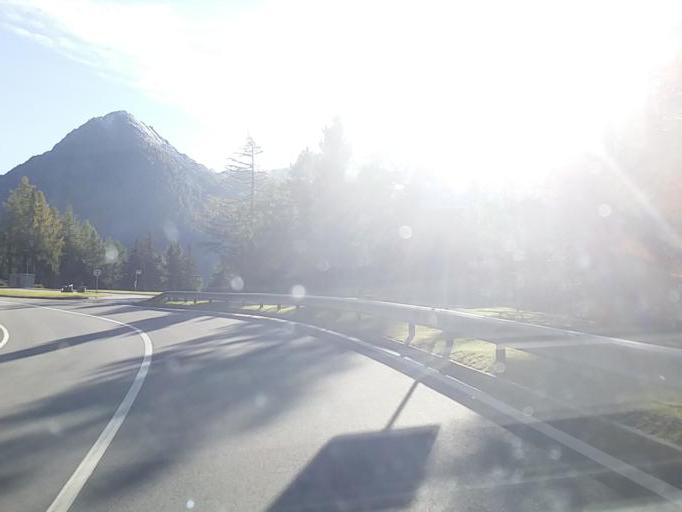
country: CH
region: Valais
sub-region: Brig District
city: Brig
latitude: 46.2841
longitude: 8.0378
